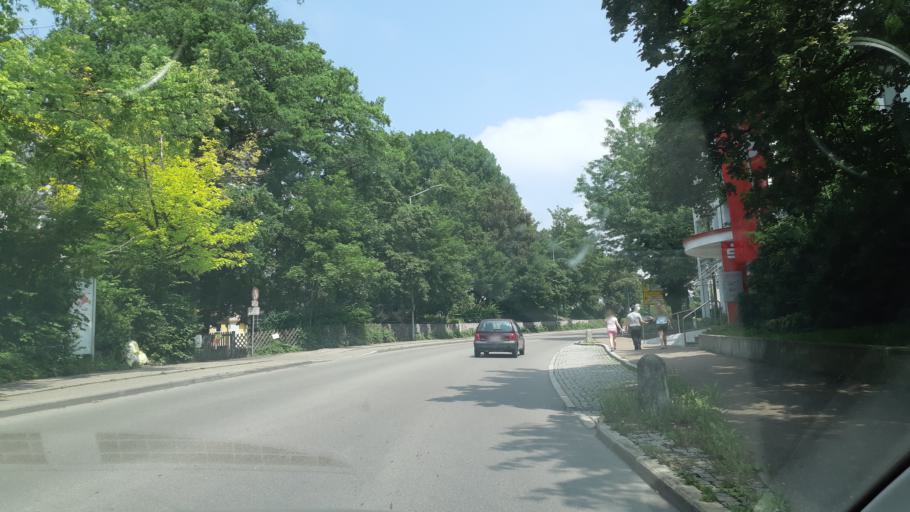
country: DE
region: Baden-Wuerttemberg
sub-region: Regierungsbezirk Stuttgart
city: Goeppingen
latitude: 48.6875
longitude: 9.6274
